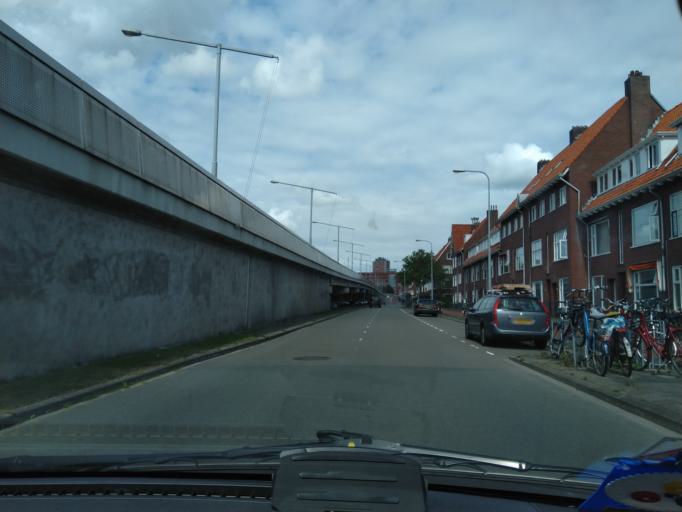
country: NL
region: Groningen
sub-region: Gemeente Groningen
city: Groningen
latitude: 53.2060
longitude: 6.5631
